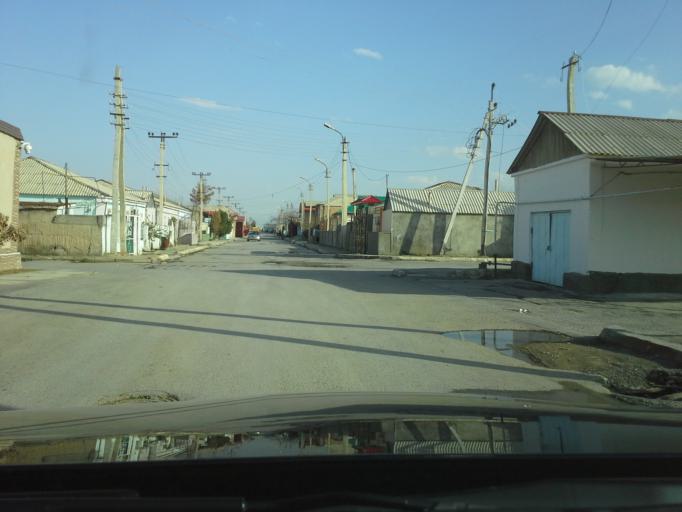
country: TM
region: Ahal
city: Abadan
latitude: 38.0199
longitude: 58.2273
